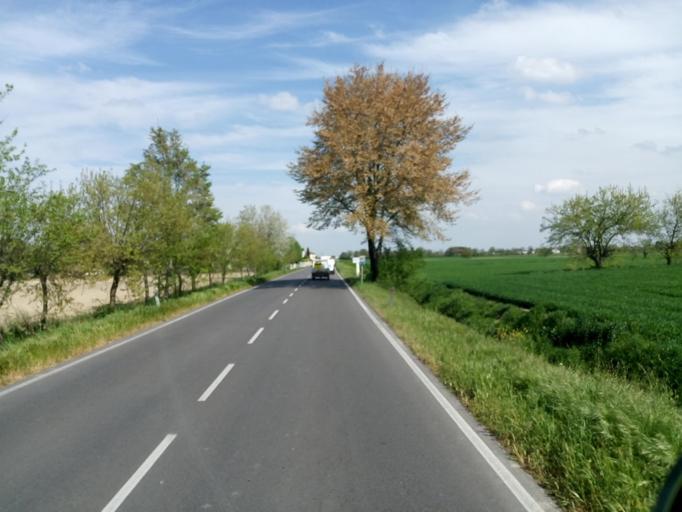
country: IT
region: Veneto
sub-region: Provincia di Verona
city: Sanguinetto
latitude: 45.1820
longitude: 11.1173
